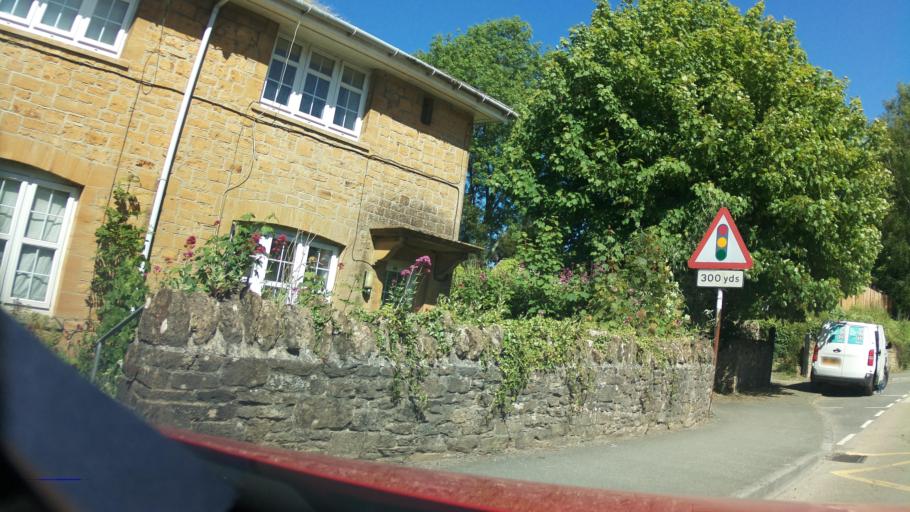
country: GB
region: England
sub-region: Somerset
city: Yeovil
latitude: 50.9193
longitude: -2.6906
